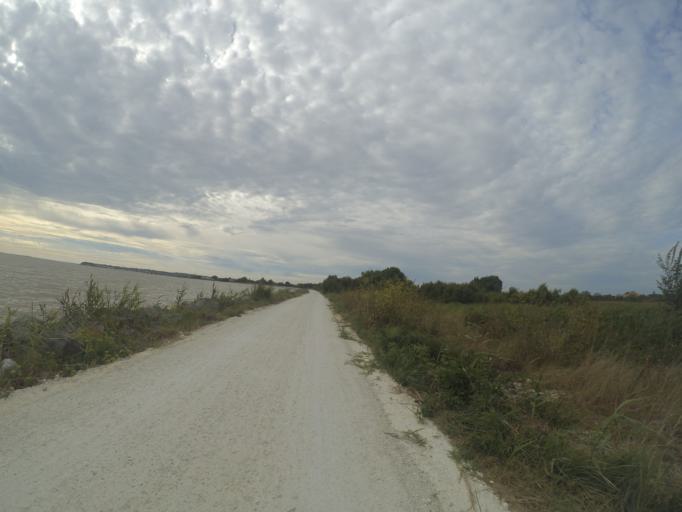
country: FR
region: Poitou-Charentes
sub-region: Departement de la Charente-Maritime
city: Meschers-sur-Gironde
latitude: 45.5482
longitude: -0.9138
